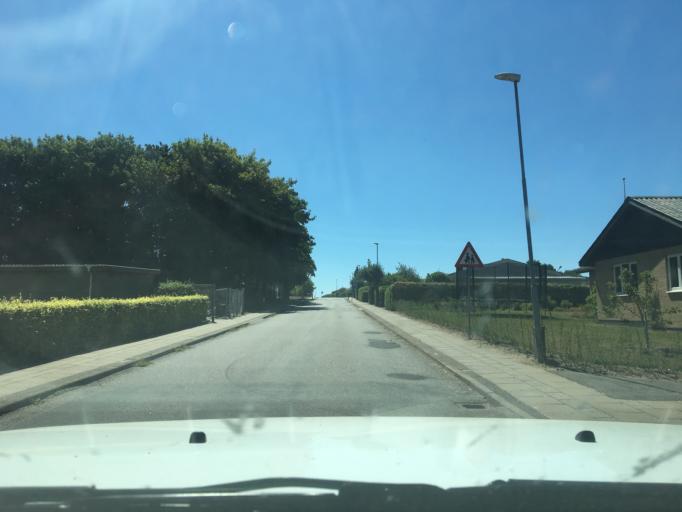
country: DK
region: Central Jutland
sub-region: Syddjurs Kommune
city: Hornslet
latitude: 56.3352
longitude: 10.3757
